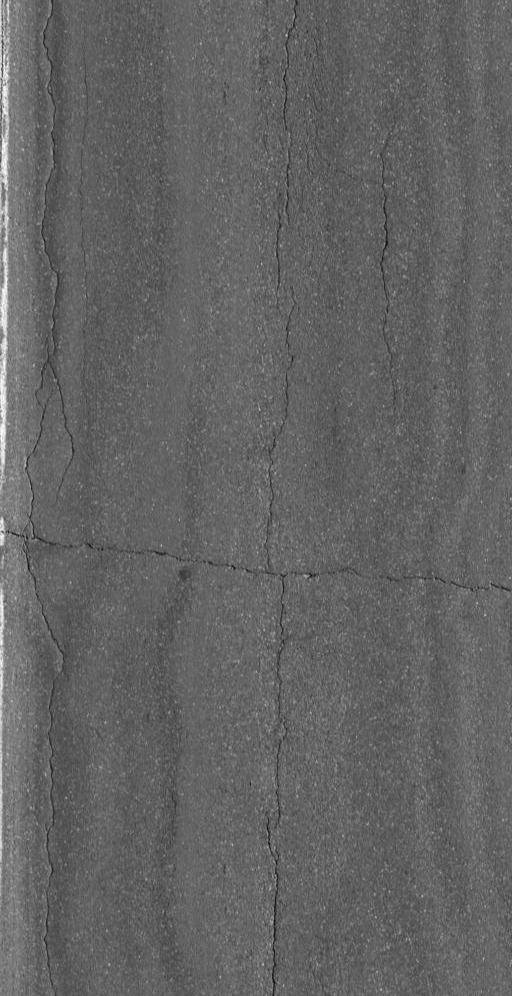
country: US
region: Vermont
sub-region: Caledonia County
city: Saint Johnsbury
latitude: 44.3970
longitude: -72.0153
